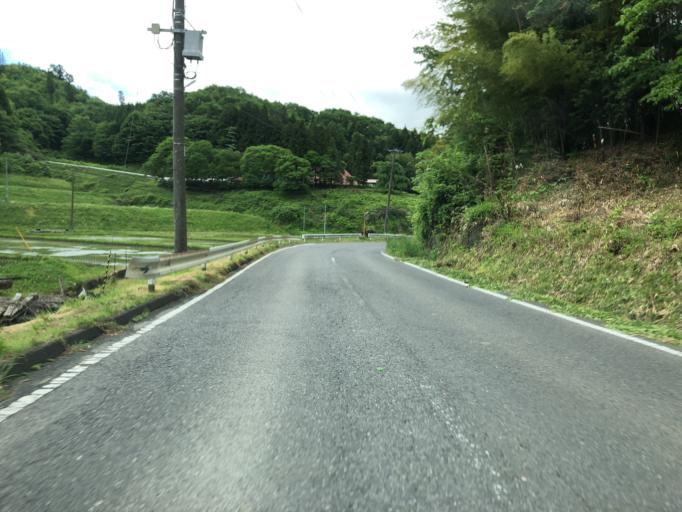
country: JP
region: Fukushima
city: Miharu
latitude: 37.4587
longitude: 140.4734
